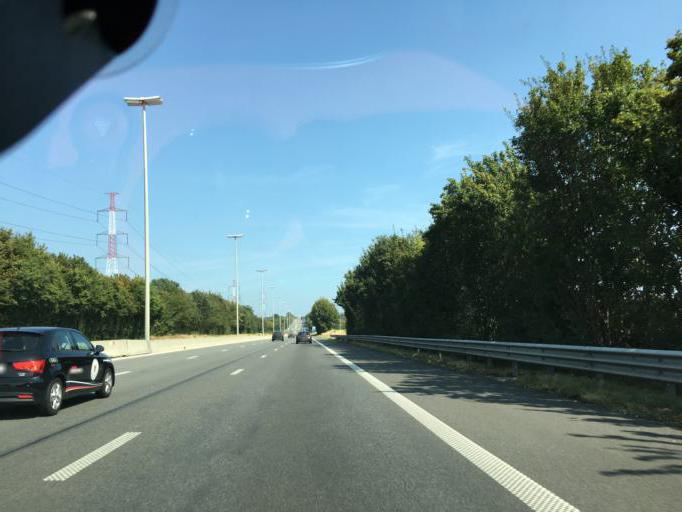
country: BE
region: Wallonia
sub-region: Province de Namur
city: Sombreffe
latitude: 50.4941
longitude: 4.6564
